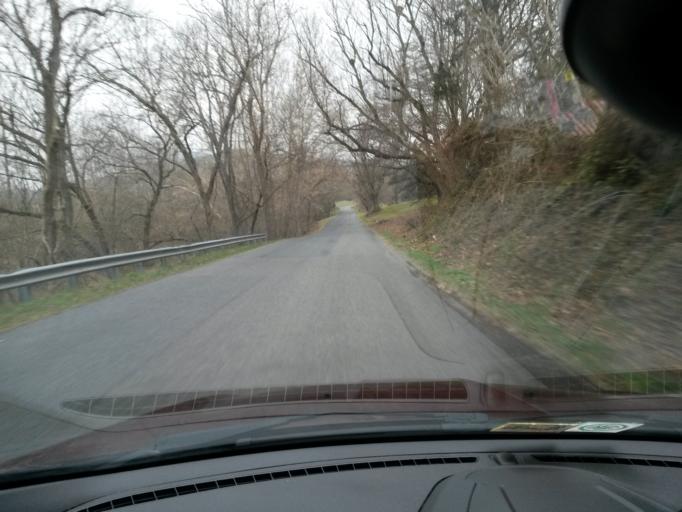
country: US
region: Virginia
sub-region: City of Lexington
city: Lexington
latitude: 37.8469
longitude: -79.4713
